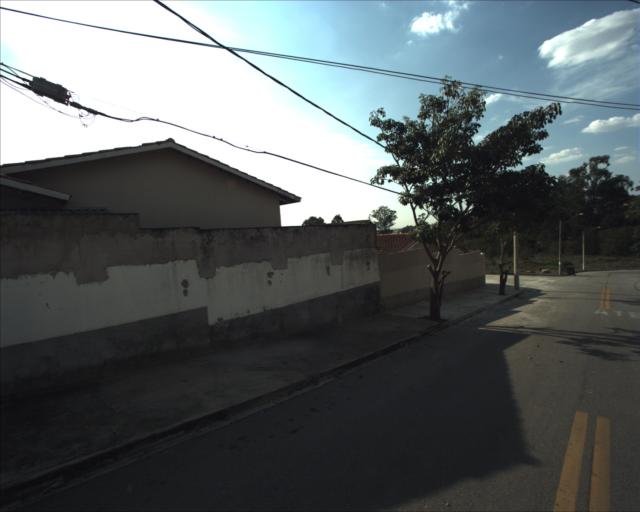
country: BR
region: Sao Paulo
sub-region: Sorocaba
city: Sorocaba
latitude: -23.4918
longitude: -47.5187
